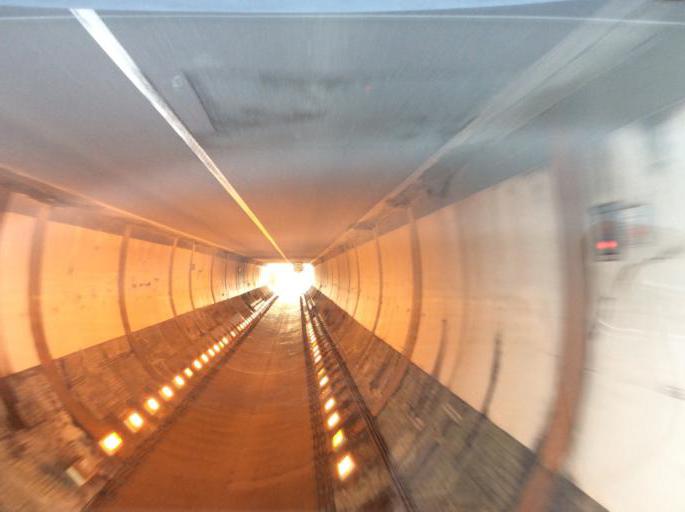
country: JP
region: Fukushima
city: Iwaki
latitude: 37.1170
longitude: 140.9993
